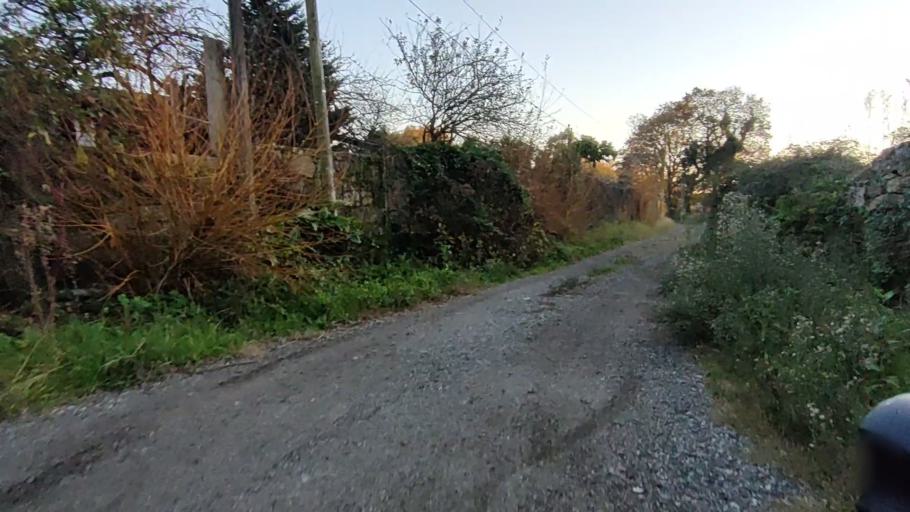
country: ES
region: Galicia
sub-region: Provincia da Coruna
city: Boiro
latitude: 42.6406
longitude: -8.8769
